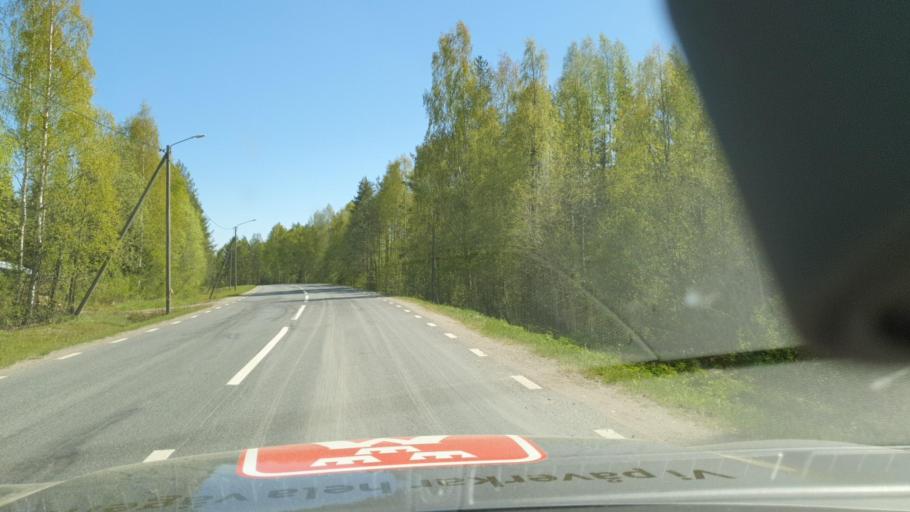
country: SE
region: Vaesternorrland
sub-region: OErnskoeldsviks Kommun
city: Ornskoldsvik
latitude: 63.5660
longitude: 18.5473
